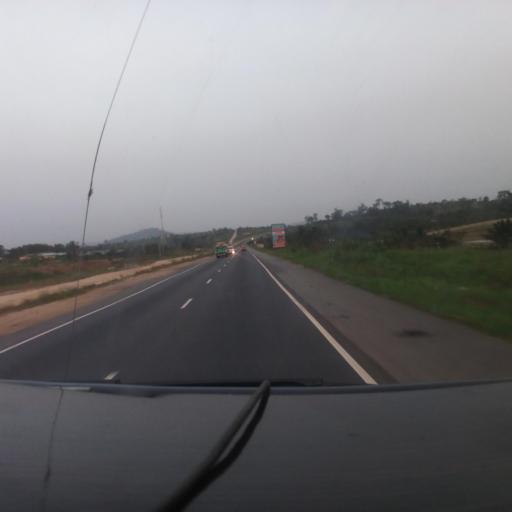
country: GH
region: Eastern
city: Nsawam
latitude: 5.8664
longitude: -0.3648
